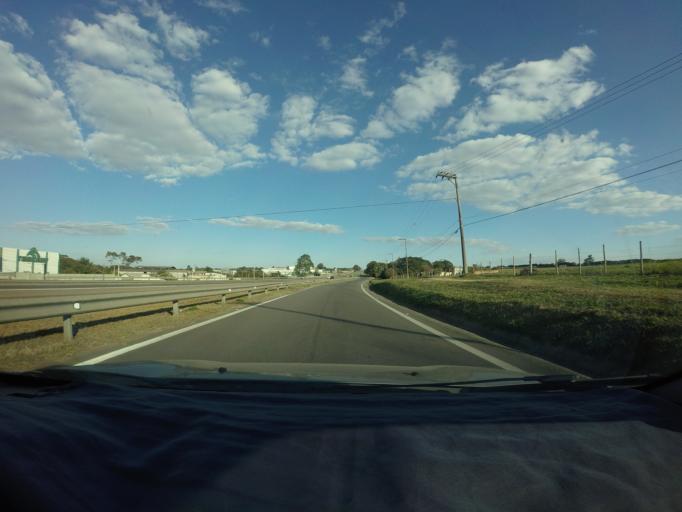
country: BR
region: Sao Paulo
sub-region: Piracicaba
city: Piracicaba
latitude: -22.7442
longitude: -47.6003
